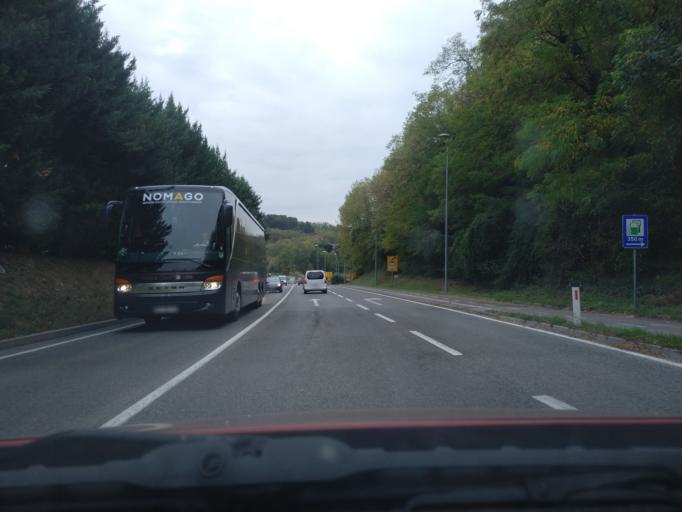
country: SI
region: Nova Gorica
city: Nova Gorica
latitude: 45.9442
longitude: 13.6436
